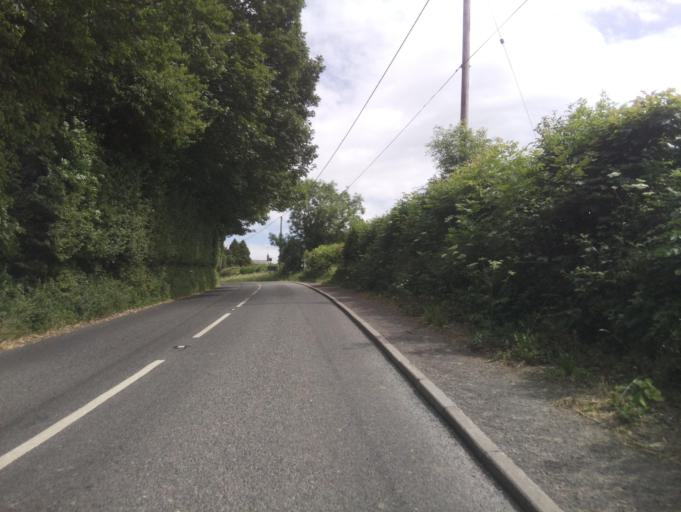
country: GB
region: England
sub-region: Somerset
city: Milborne Port
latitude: 51.0093
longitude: -2.4750
